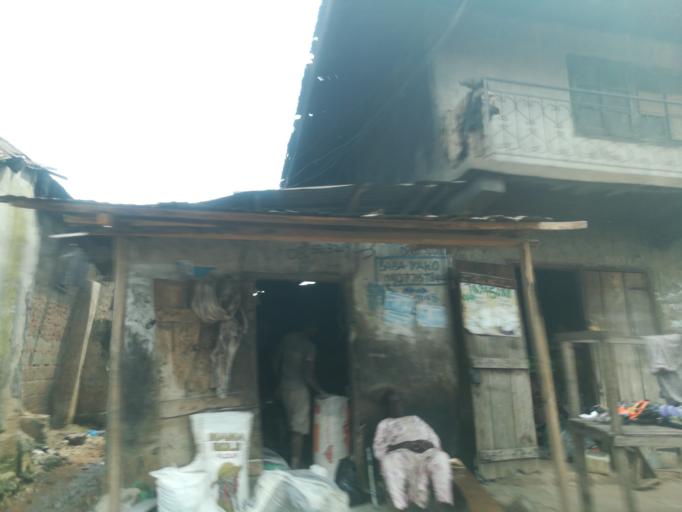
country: NG
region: Oyo
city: Ibadan
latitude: 7.3888
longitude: 3.9088
